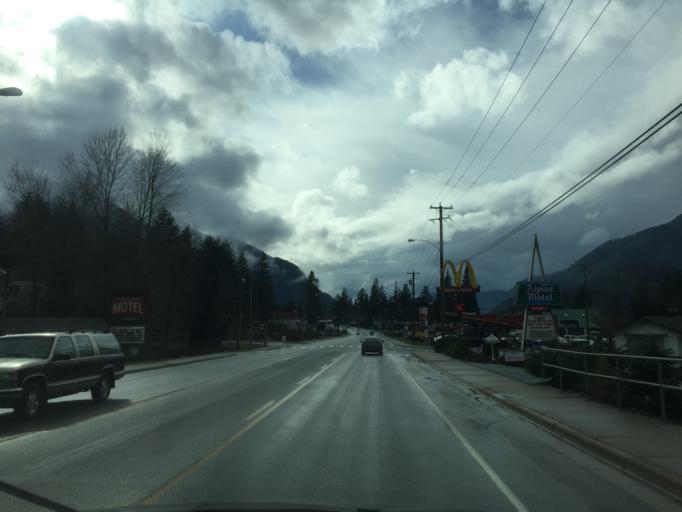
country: CA
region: British Columbia
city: Hope
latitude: 49.3755
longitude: -121.4321
